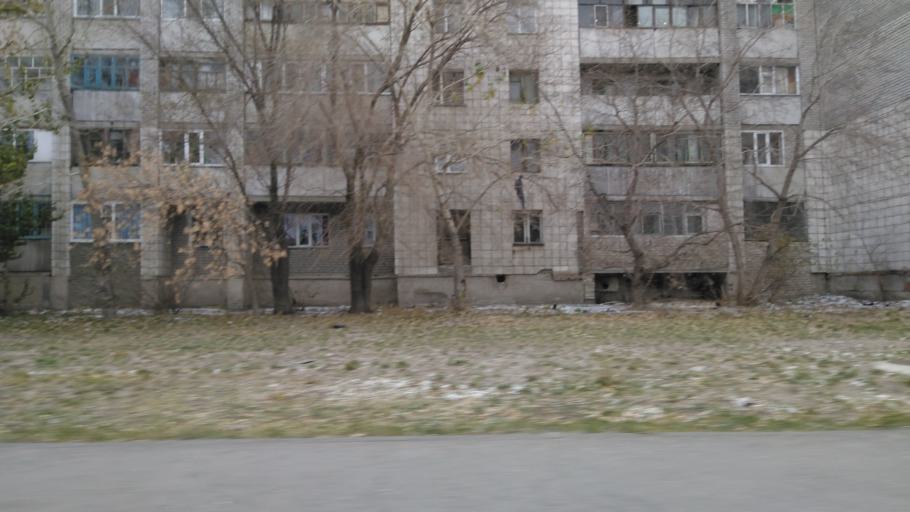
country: KZ
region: Pavlodar
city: Pavlodar
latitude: 52.2771
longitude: 76.9621
